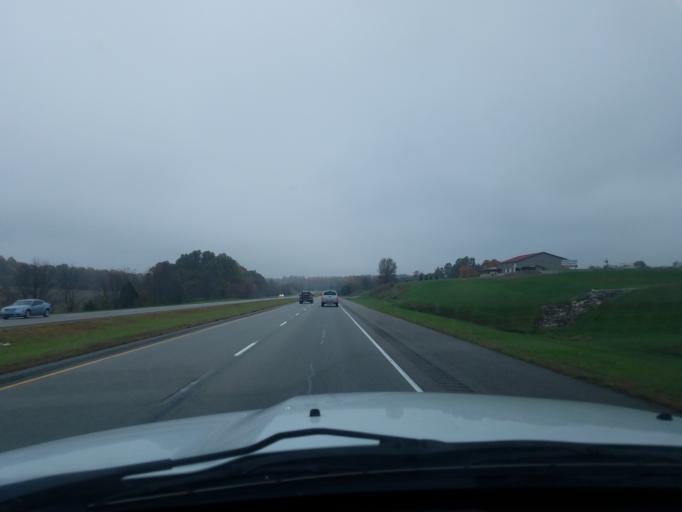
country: US
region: Kentucky
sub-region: Hardin County
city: Elizabethtown
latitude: 37.6506
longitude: -85.8373
